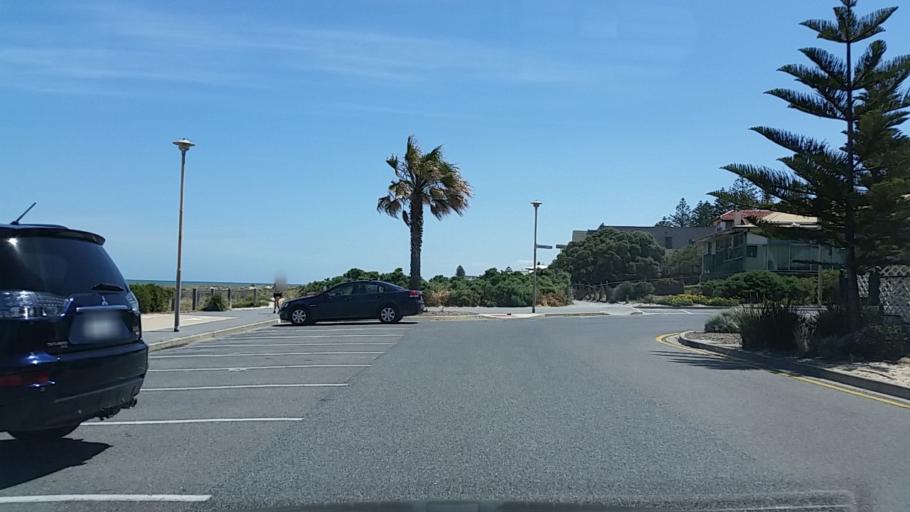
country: AU
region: South Australia
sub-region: Charles Sturt
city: Grange
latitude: -34.9001
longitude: 138.4888
